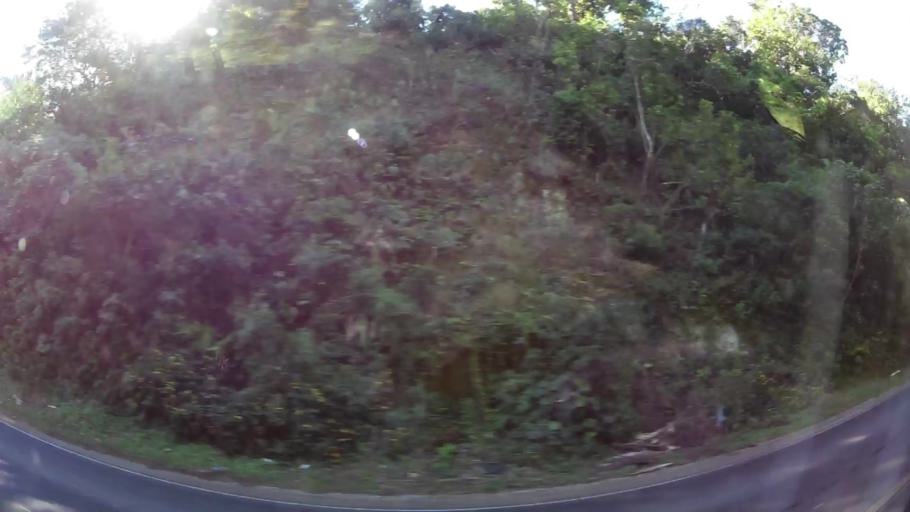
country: SV
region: Sonsonate
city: Juayua
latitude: 13.8523
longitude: -89.7776
